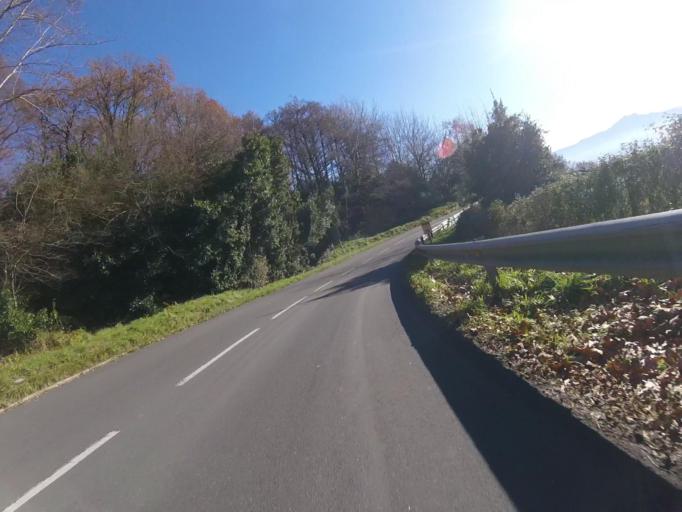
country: ES
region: Basque Country
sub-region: Provincia de Guipuzcoa
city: Fuenterrabia
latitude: 43.3701
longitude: -1.8143
